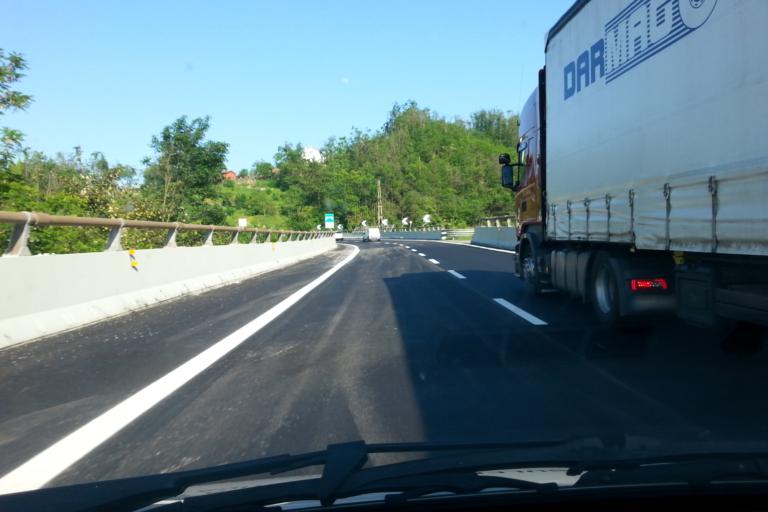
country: IT
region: Liguria
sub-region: Provincia di Savona
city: Altare
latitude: 44.3346
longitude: 8.3351
